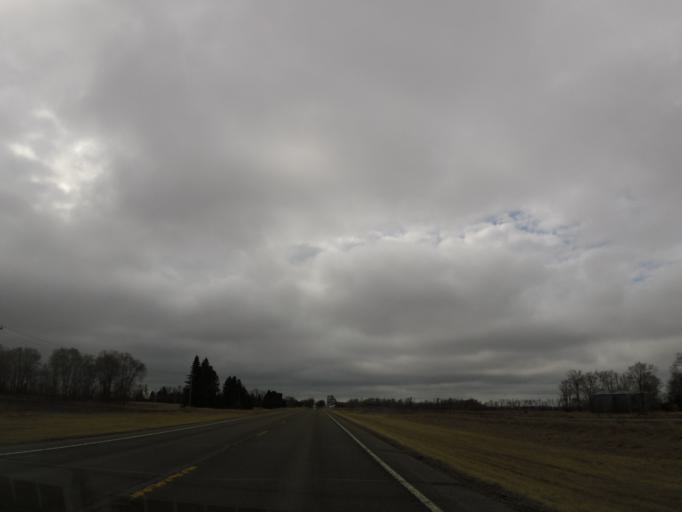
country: US
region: North Dakota
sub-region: Cass County
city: Casselton
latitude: 47.1168
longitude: -97.2179
